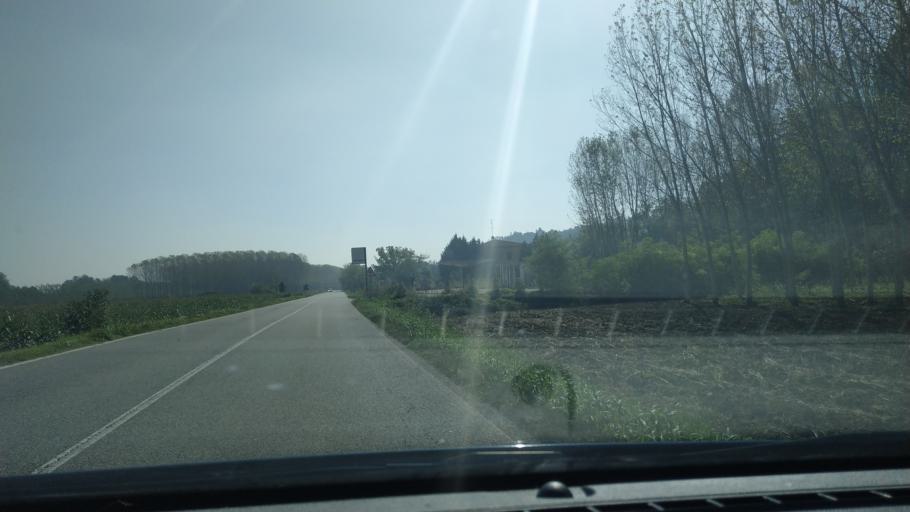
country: IT
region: Piedmont
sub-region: Provincia di Alessandria
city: Pomaro Monferrato
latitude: 45.0656
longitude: 8.5973
